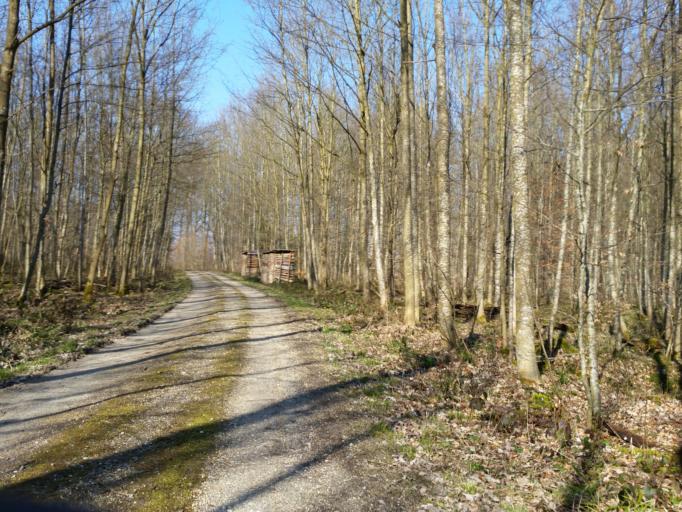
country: CH
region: Thurgau
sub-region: Arbon District
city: Uttwil
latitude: 47.5714
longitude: 9.3405
